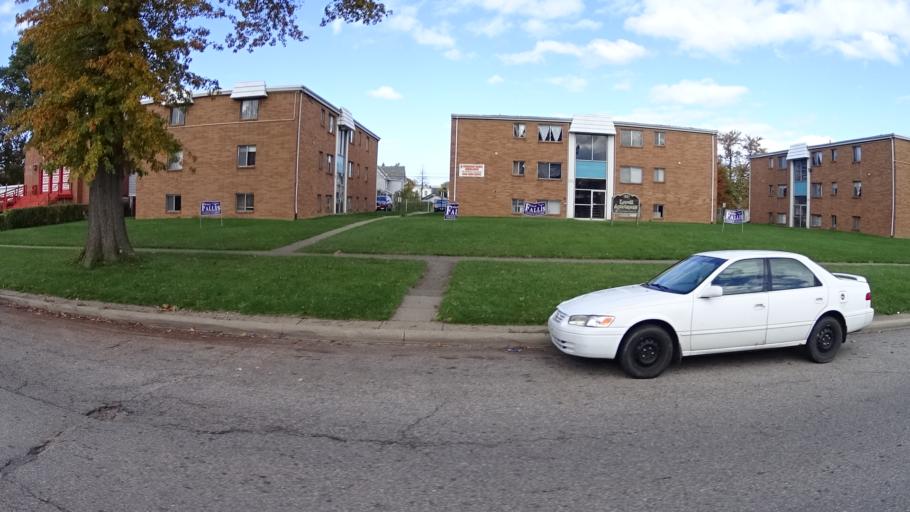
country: US
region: Ohio
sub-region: Lorain County
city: Sheffield
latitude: 41.4422
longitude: -82.1349
